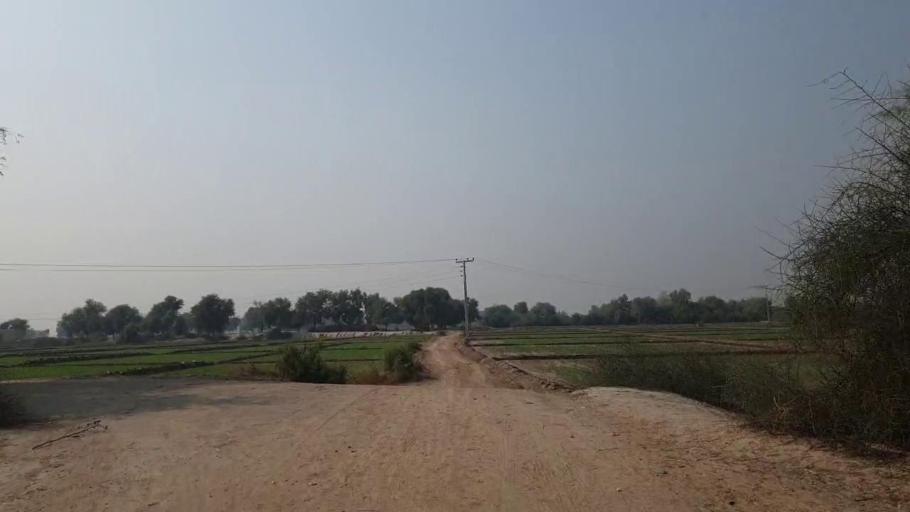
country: PK
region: Sindh
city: Bhan
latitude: 26.5147
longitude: 67.7418
